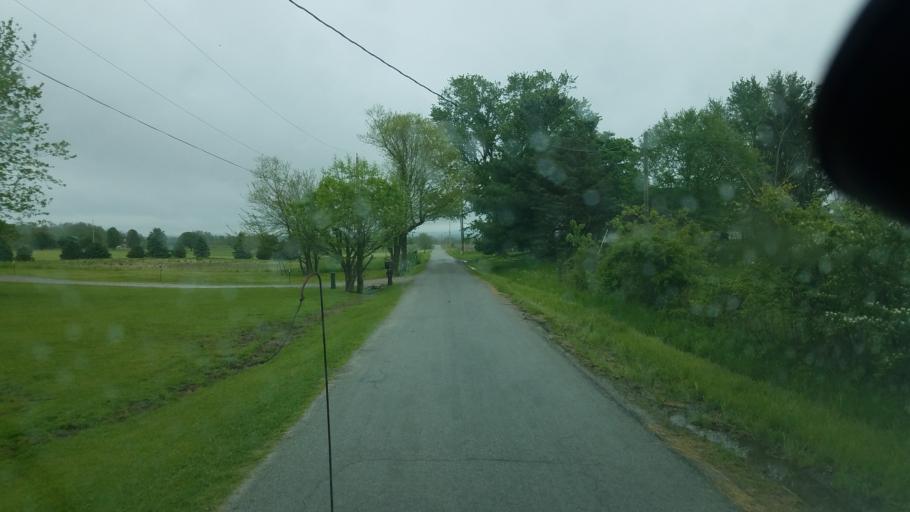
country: US
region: Ohio
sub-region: Highland County
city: Greenfield
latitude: 39.3364
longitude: -83.4300
